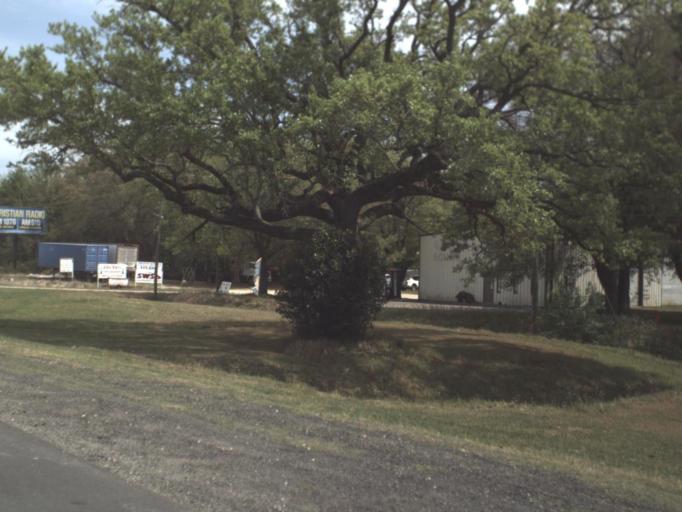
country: US
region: Florida
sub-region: Escambia County
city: Ensley
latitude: 30.5341
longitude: -87.3041
